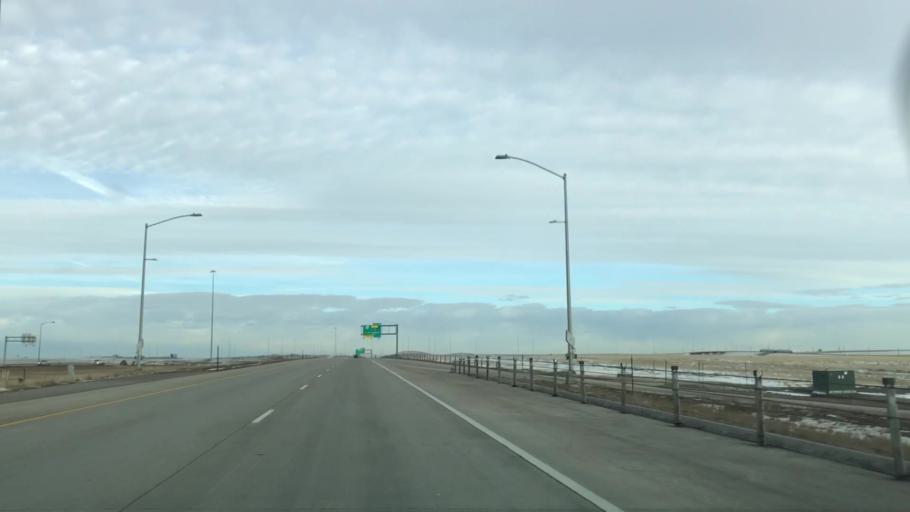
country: US
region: Colorado
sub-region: Adams County
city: Aurora
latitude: 39.8340
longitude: -104.7656
